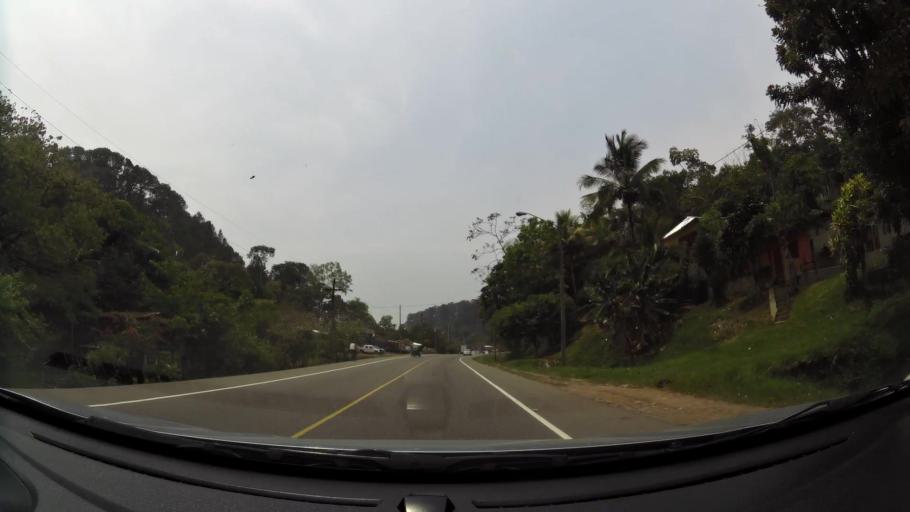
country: HN
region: Cortes
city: La Guama
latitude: 14.8867
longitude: -87.9379
